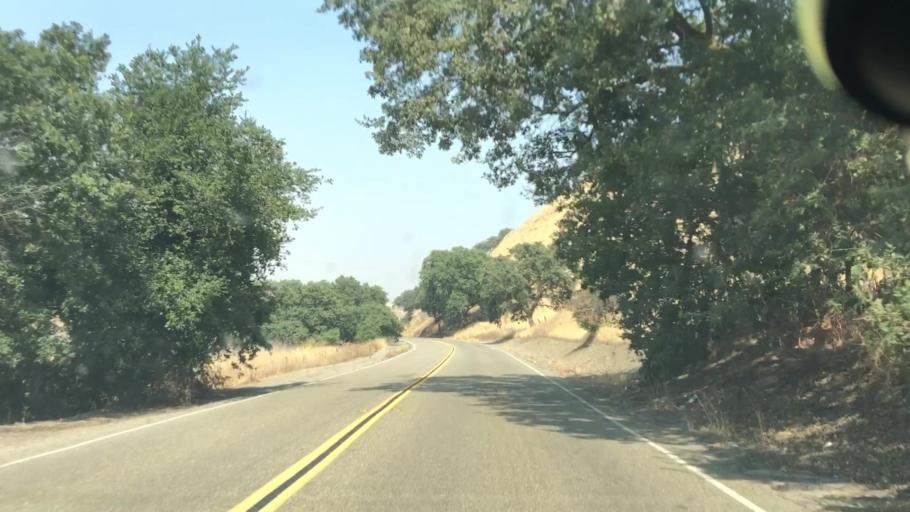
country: US
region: California
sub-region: Alameda County
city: Livermore
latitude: 37.6426
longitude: -121.6353
